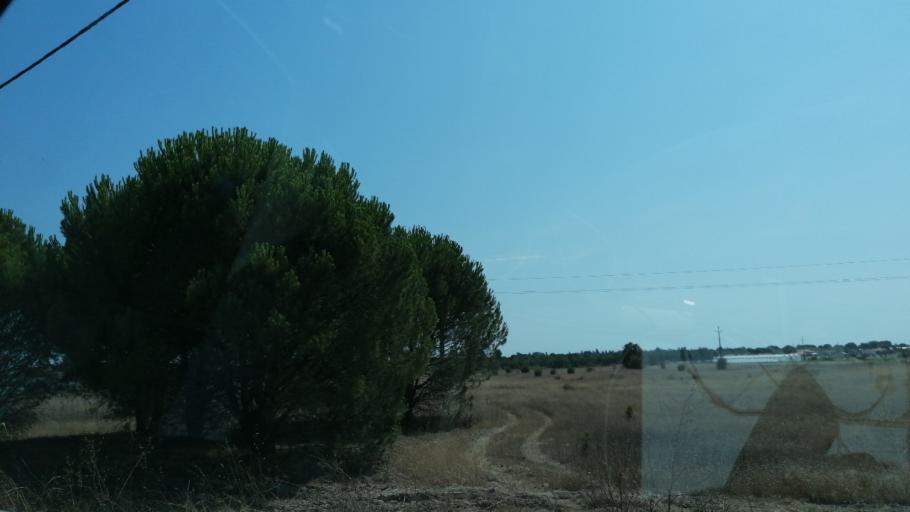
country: PT
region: Santarem
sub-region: Benavente
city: Poceirao
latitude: 38.7378
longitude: -8.6551
